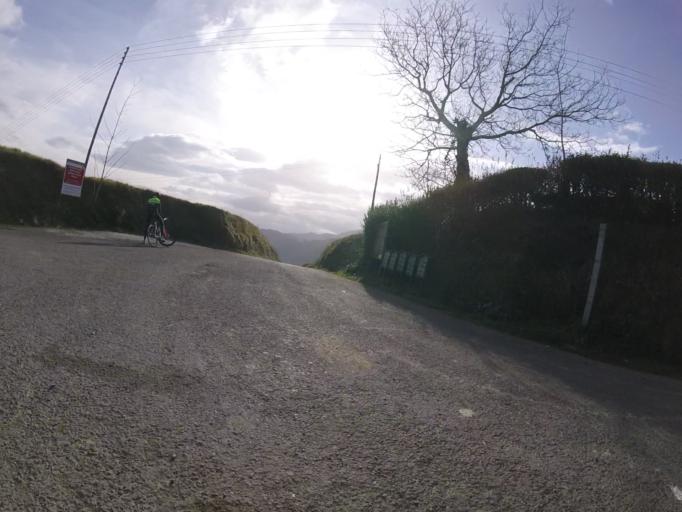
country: ES
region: Basque Country
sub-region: Provincia de Guipuzcoa
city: Larraul
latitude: 43.2025
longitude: -2.1349
